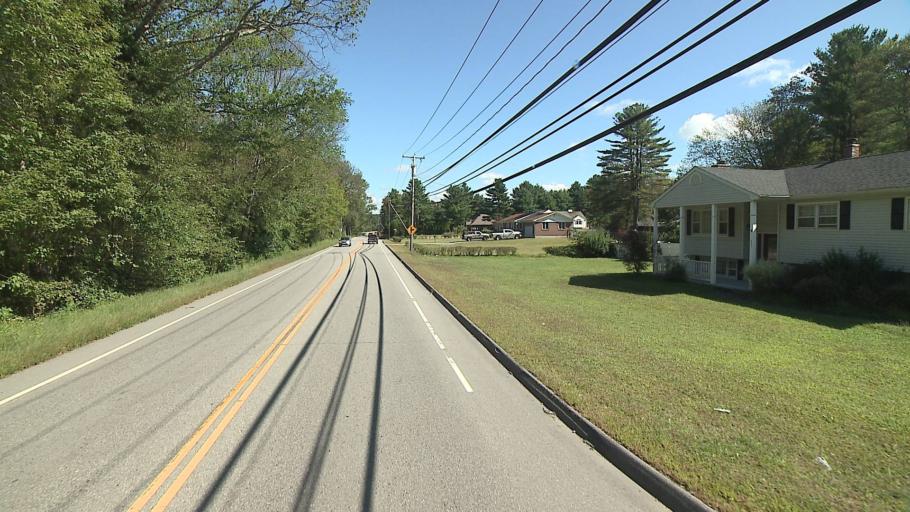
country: US
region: Connecticut
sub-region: Windham County
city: East Brooklyn
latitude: 41.7738
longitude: -71.8964
